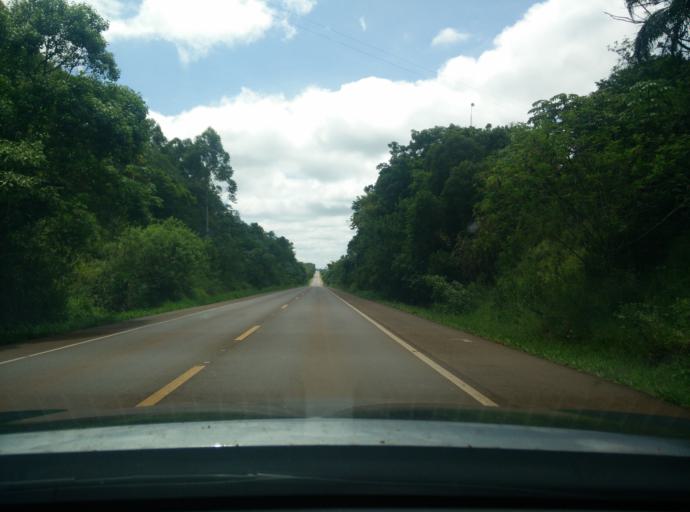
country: BR
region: Parana
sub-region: Campo Mourao
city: Campo Mourao
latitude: -23.9801
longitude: -52.5375
